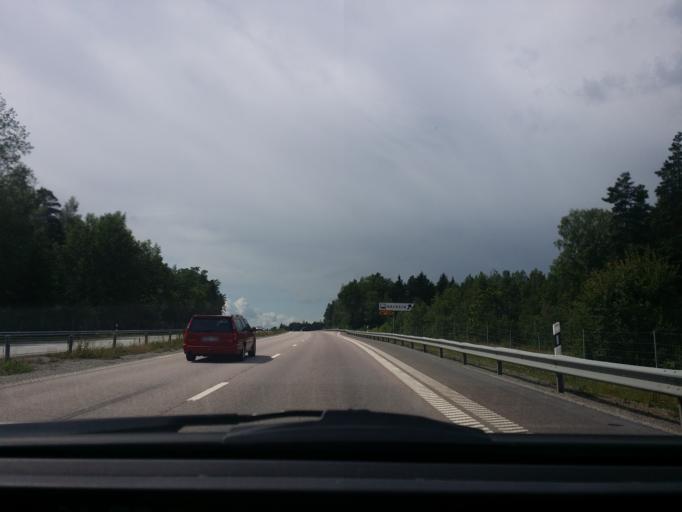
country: SE
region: Vaestmanland
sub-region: Vasteras
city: Vasteras
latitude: 59.6038
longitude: 16.4455
